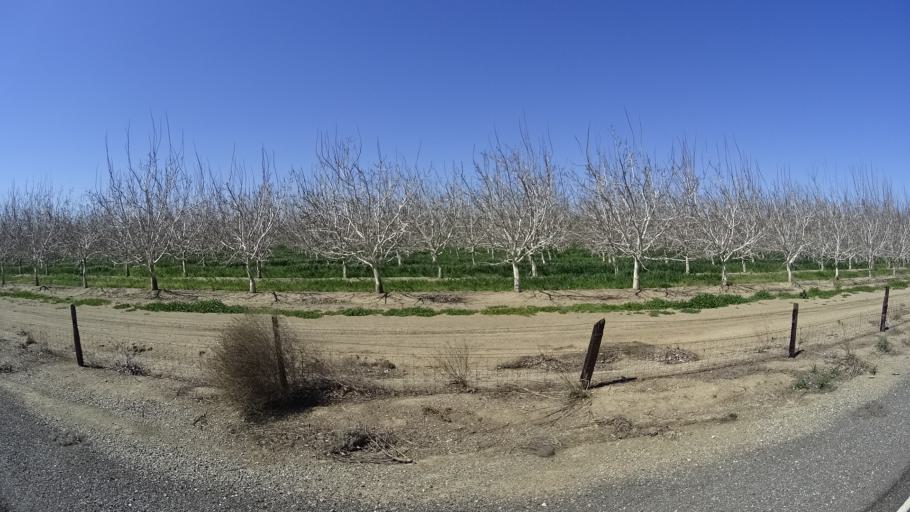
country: US
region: California
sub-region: Glenn County
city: Willows
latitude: 39.6221
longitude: -122.2500
